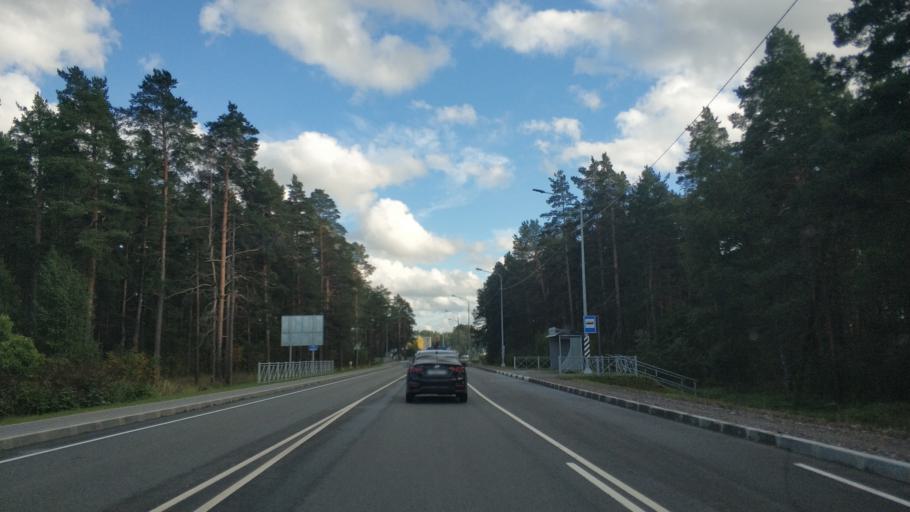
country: RU
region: Leningrad
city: Priozersk
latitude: 61.0048
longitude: 30.1796
